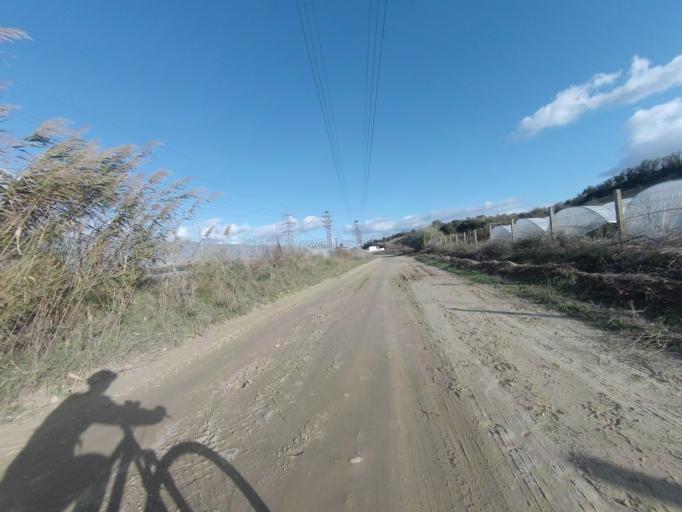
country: ES
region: Andalusia
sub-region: Provincia de Huelva
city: Moguer
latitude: 37.2655
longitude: -6.8531
